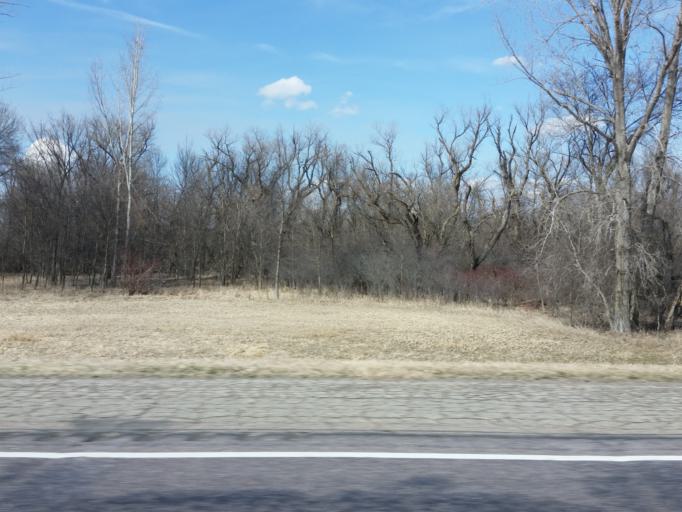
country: US
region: Minnesota
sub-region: Lac qui Parle County
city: Madison
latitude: 44.9358
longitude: -96.3217
